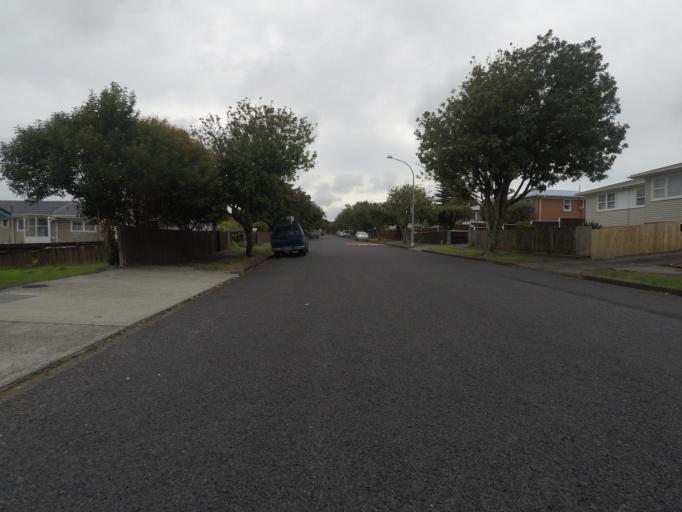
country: NZ
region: Auckland
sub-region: Auckland
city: Rosebank
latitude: -36.8921
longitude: 174.6777
